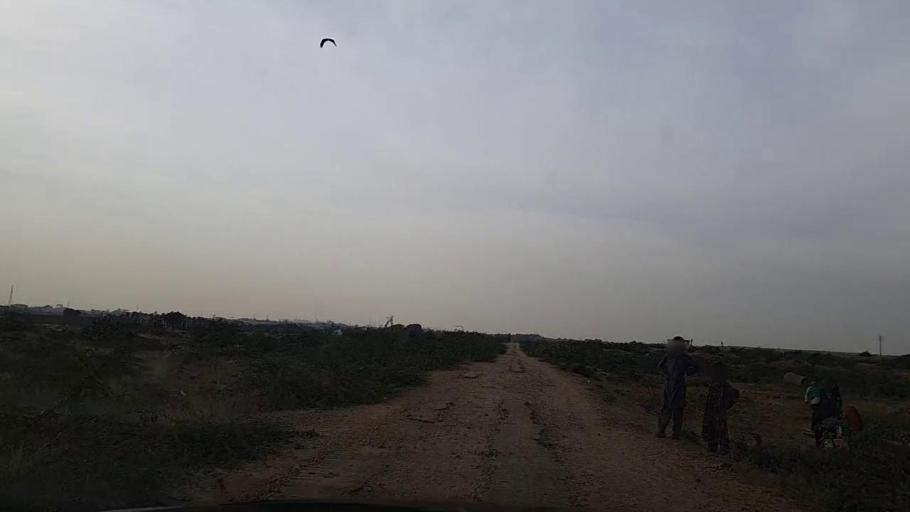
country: PK
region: Sindh
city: Gharo
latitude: 24.7930
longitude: 67.5443
